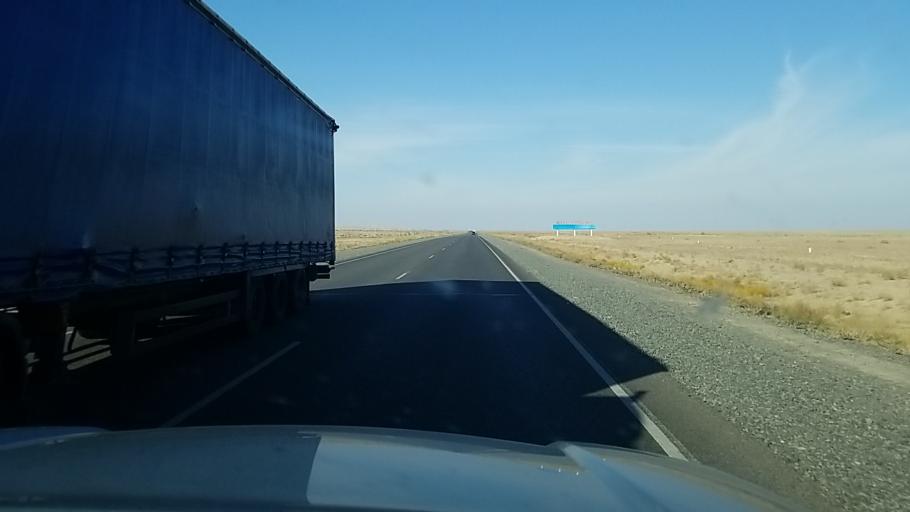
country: KZ
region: Qyzylorda
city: Ayteke Bi
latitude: 46.0674
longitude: 62.0995
